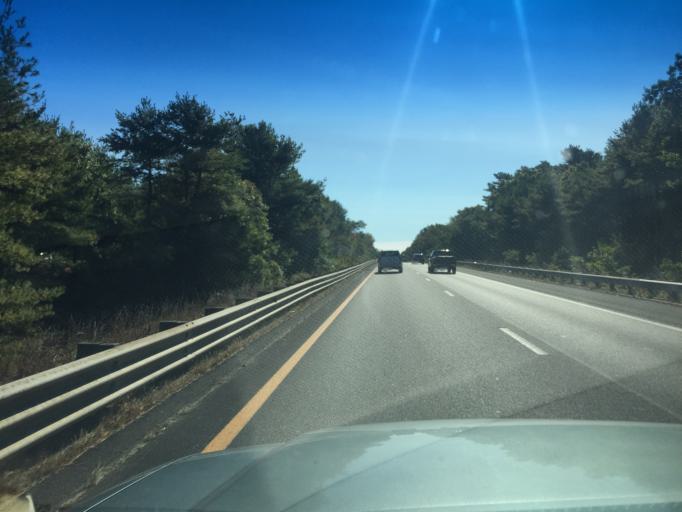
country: US
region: Massachusetts
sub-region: Plymouth County
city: West Wareham
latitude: 41.7933
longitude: -70.7503
